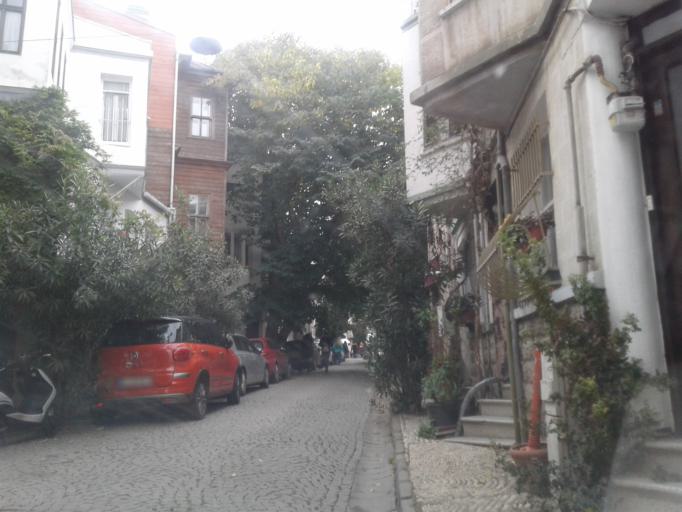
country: TR
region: Istanbul
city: UEskuedar
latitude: 41.0360
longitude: 29.0305
